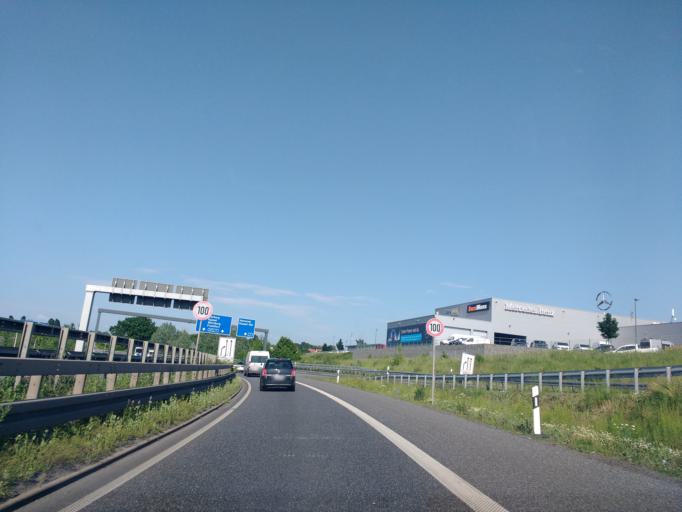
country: DE
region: Hesse
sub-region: Regierungsbezirk Kassel
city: Lohfelden
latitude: 51.2711
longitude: 9.5272
